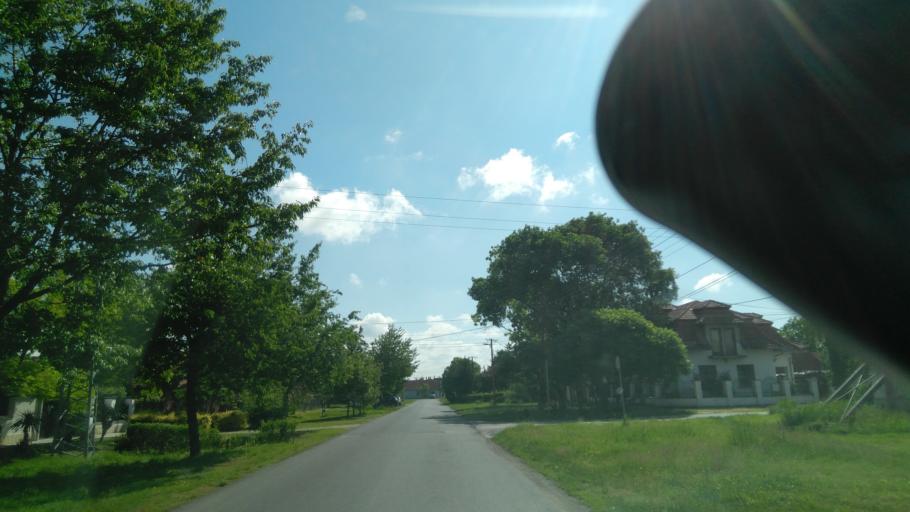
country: HU
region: Bekes
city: Bekes
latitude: 46.7762
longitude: 21.1193
